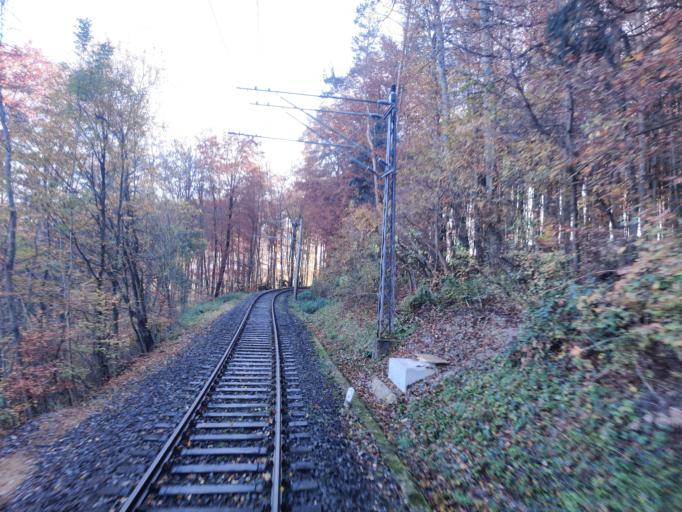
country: AT
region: Styria
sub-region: Politischer Bezirk Suedoststeiermark
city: Maierdorf
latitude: 46.9287
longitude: 15.8539
